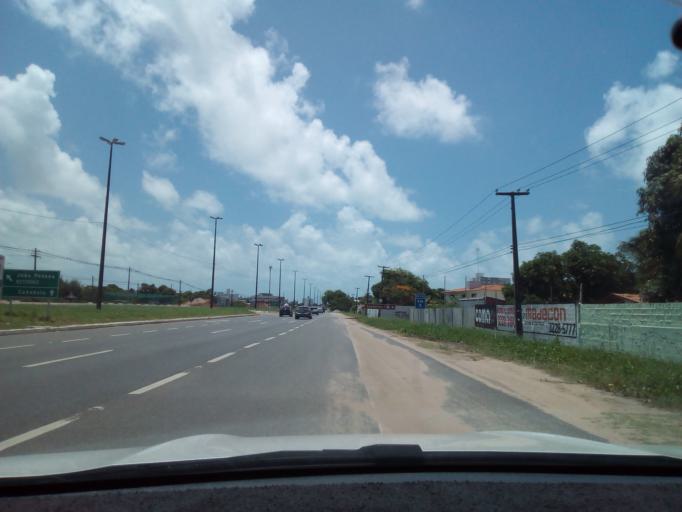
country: BR
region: Paraiba
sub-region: Cabedelo
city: Cabedelo
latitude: -7.0126
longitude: -34.8322
